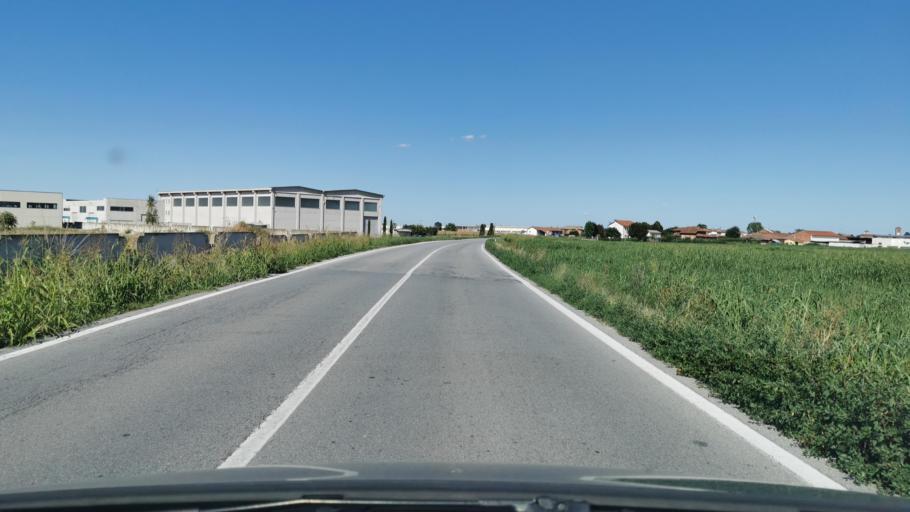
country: IT
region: Piedmont
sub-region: Provincia di Cuneo
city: Genola
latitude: 44.5854
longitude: 7.6481
